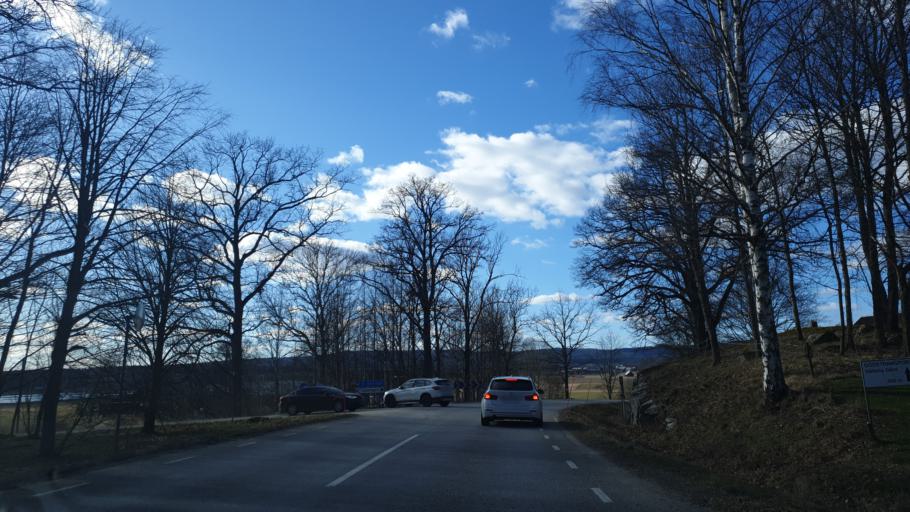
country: SE
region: OErebro
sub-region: Orebro Kommun
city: Garphyttan
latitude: 59.3381
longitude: 15.0638
